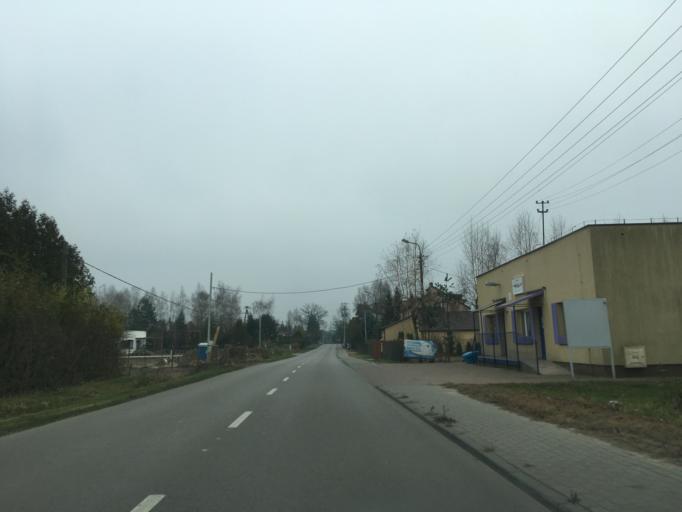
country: PL
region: Masovian Voivodeship
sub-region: Powiat piaseczynski
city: Lesznowola
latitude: 52.0527
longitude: 20.9276
